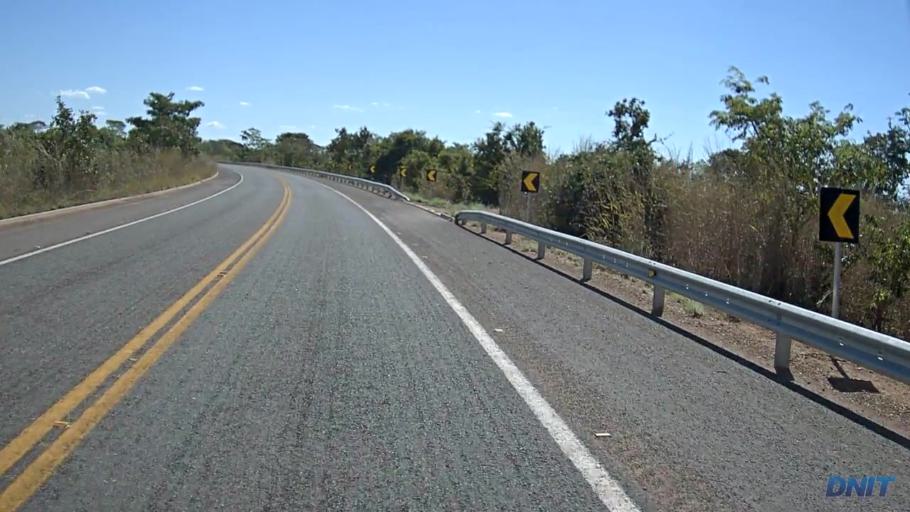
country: BR
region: Goias
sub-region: Sao Miguel Do Araguaia
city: Sao Miguel do Araguaia
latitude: -13.2408
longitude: -50.5404
